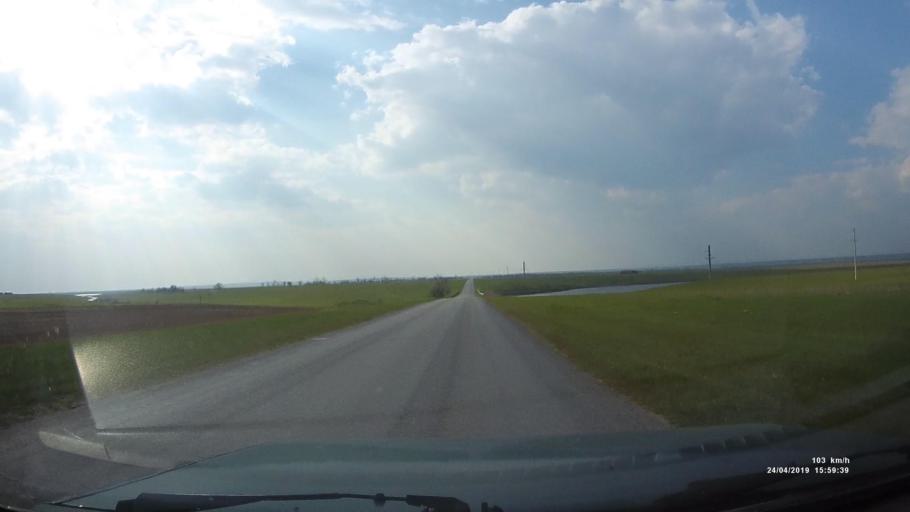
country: RU
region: Rostov
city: Sovetskoye
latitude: 46.6256
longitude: 42.4676
